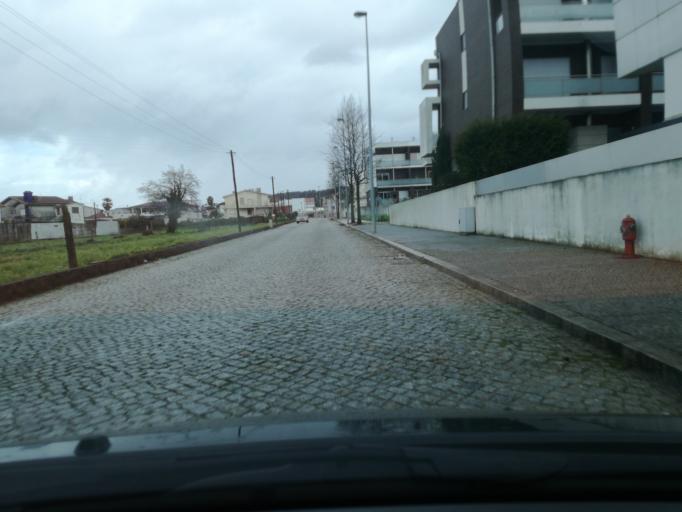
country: PT
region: Porto
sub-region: Valongo
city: Ermesinde
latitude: 41.2480
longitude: -8.5495
